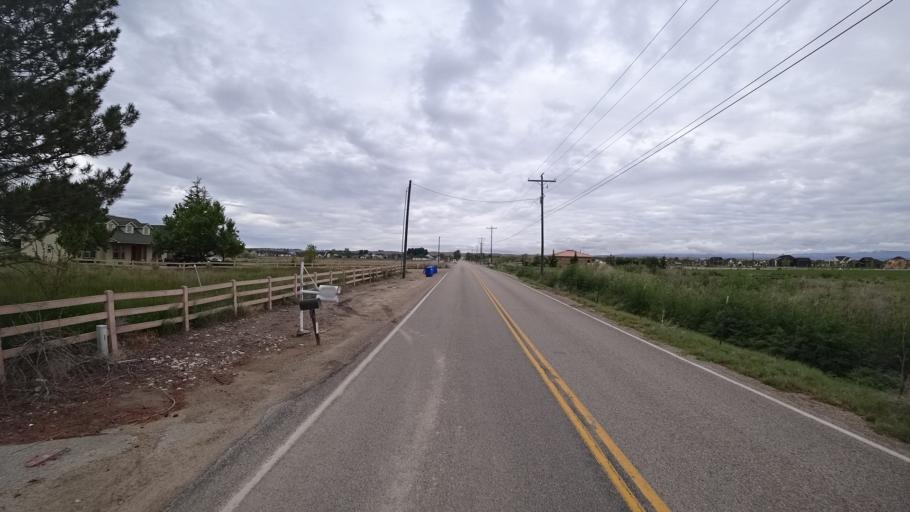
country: US
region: Idaho
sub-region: Ada County
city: Star
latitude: 43.6984
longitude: -116.4437
